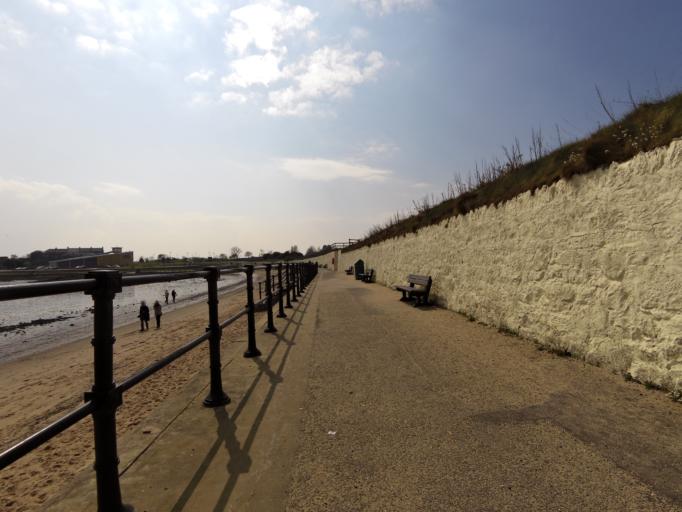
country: GB
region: Scotland
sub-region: Fife
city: Burntisland
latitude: 56.0618
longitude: -3.2242
